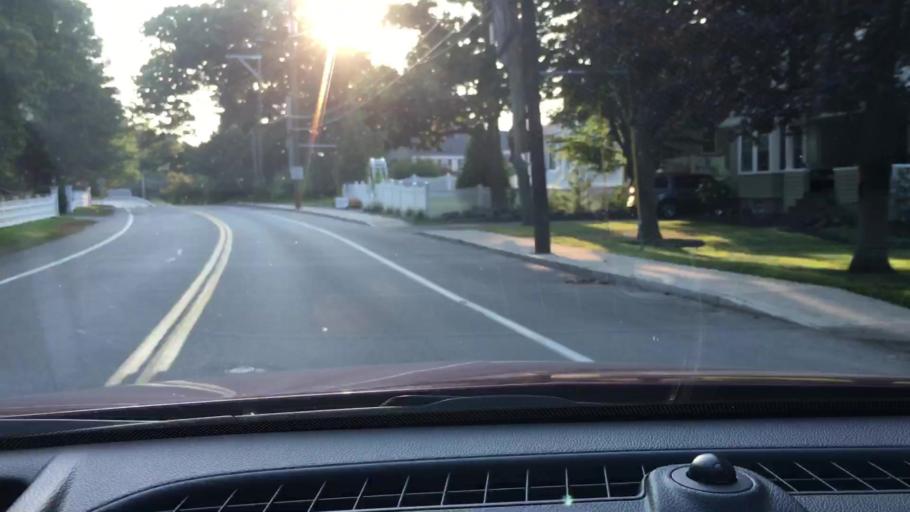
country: US
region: New Hampshire
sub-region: Rockingham County
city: Portsmouth
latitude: 43.0625
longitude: -70.7713
